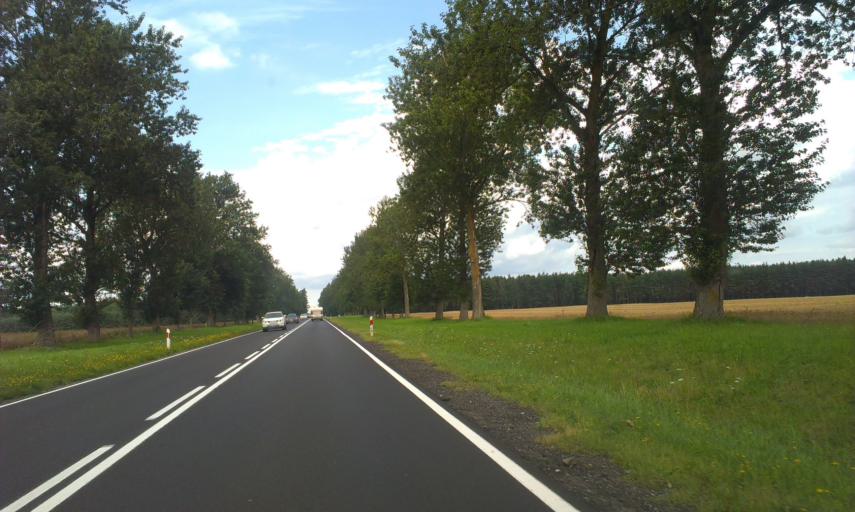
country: PL
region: West Pomeranian Voivodeship
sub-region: Powiat koszalinski
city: Bobolice
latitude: 54.0529
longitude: 16.4267
